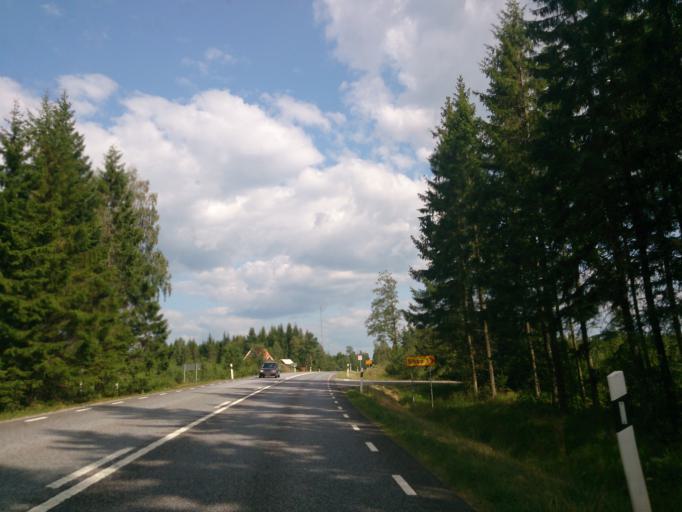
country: SE
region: Joenkoeping
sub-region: Gislaveds Kommun
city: Smalandsstenar
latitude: 57.1606
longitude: 13.4715
